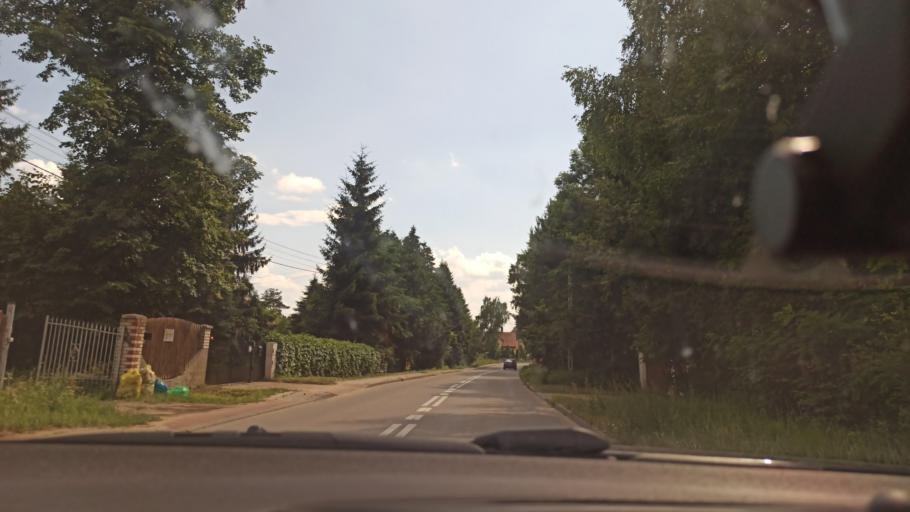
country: PL
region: Podlasie
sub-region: Powiat bialostocki
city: Turosn Koscielna
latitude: 53.0672
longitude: 23.0997
